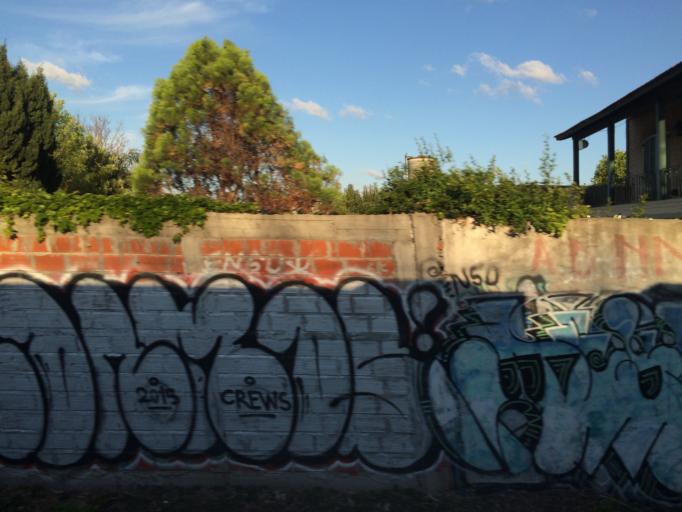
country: AR
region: Buenos Aires
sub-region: Partido de Lomas de Zamora
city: Lomas de Zamora
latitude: -34.7527
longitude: -58.3963
